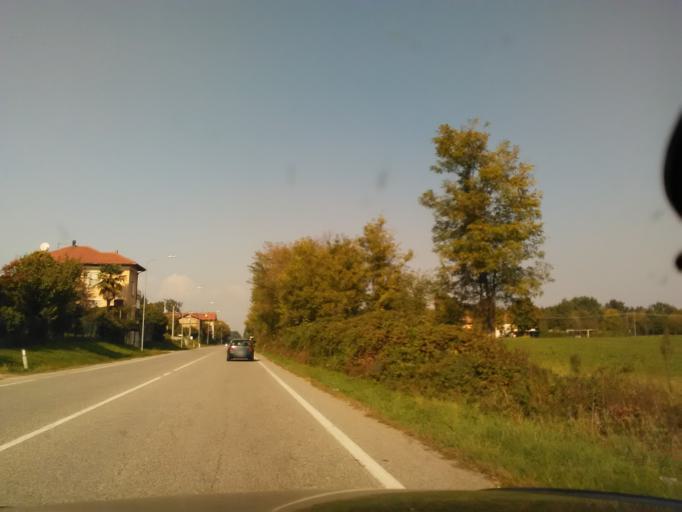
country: IT
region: Piedmont
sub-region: Provincia di Biella
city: Salussola
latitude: 45.4365
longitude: 8.1122
